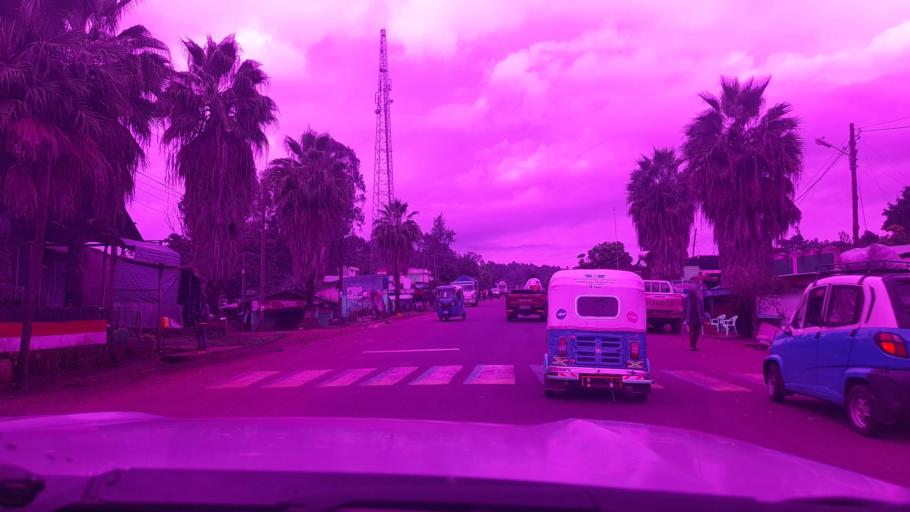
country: ET
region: Oromiya
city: Jima
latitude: 7.9257
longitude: 37.4181
